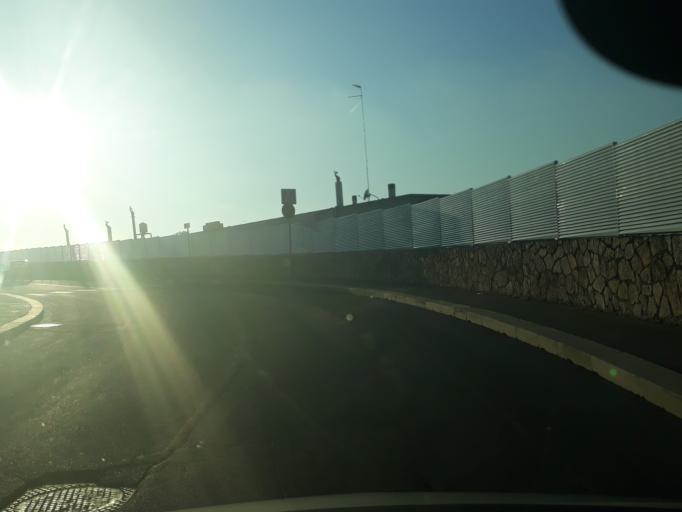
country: IT
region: Apulia
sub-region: Provincia di Bari
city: Locorotondo
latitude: 40.7605
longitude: 17.3271
